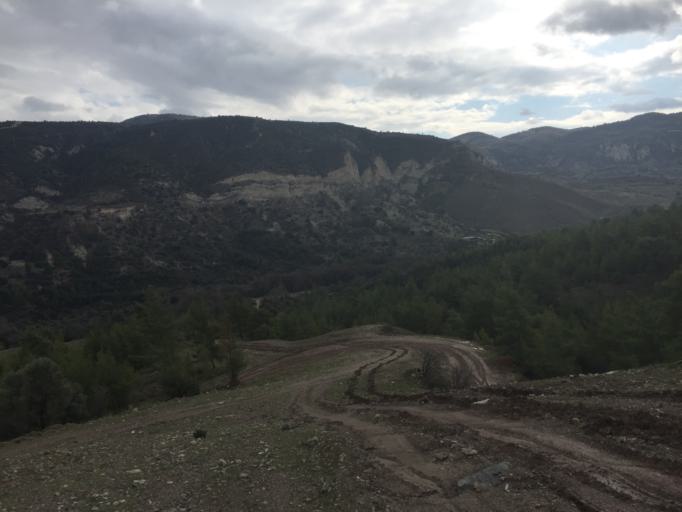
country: CY
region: Limassol
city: Pachna
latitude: 34.8854
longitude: 32.6698
